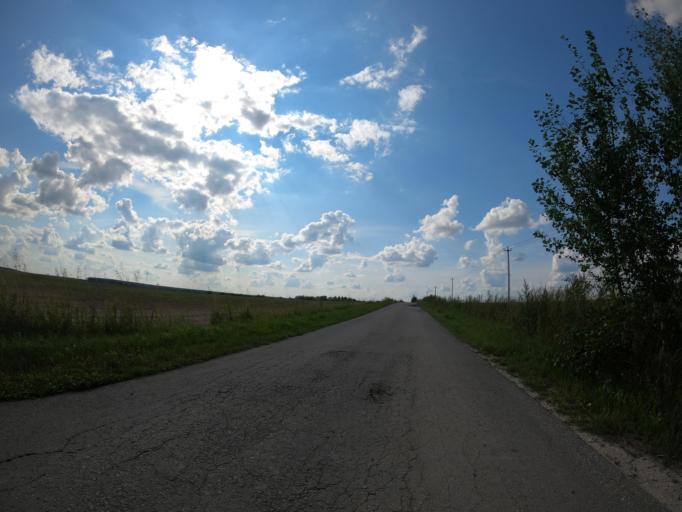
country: RU
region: Moskovskaya
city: Troitskoye
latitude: 55.2379
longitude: 38.5029
